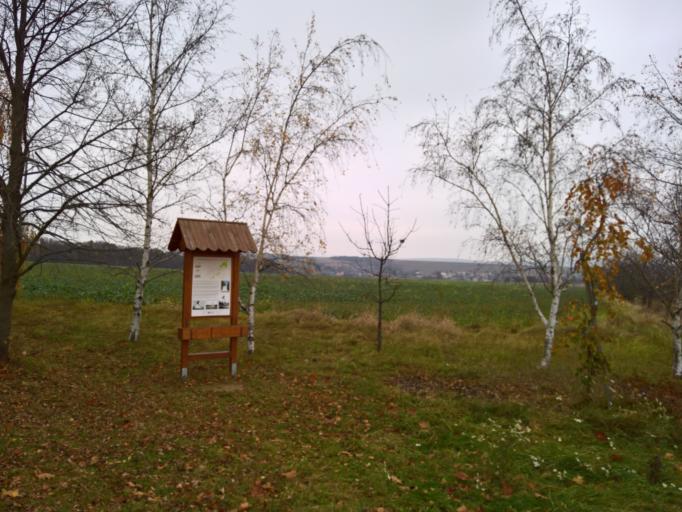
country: SK
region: Nitriansky
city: Zlate Moravce
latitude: 48.3255
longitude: 18.3956
